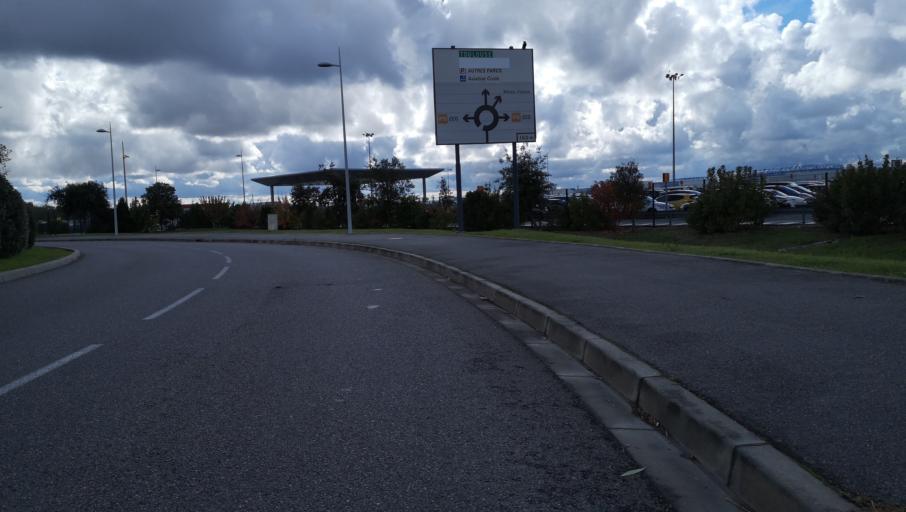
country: FR
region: Midi-Pyrenees
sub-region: Departement de la Haute-Garonne
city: Blagnac
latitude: 43.6387
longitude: 1.3641
